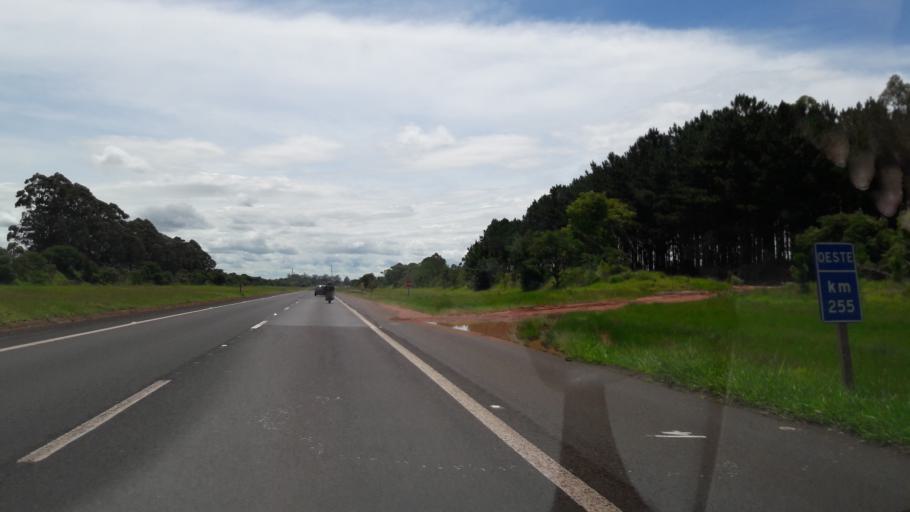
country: BR
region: Sao Paulo
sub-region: Avare
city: Avare
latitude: -22.9407
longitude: -48.9365
